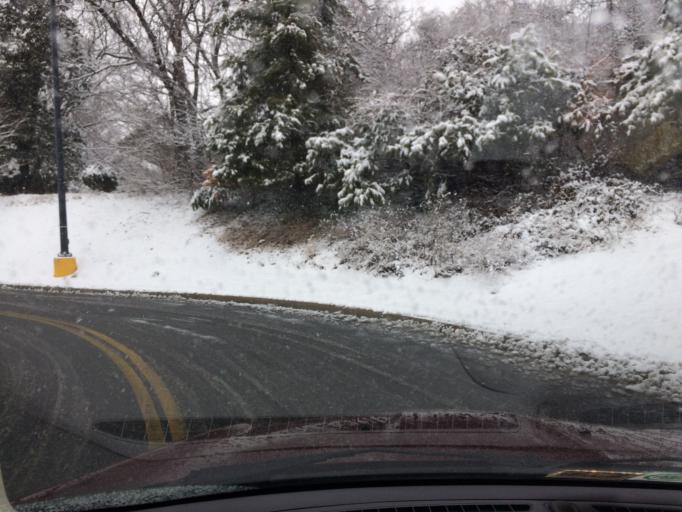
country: US
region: Virginia
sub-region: Amherst County
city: Madison Heights
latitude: 37.4628
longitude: -79.1179
